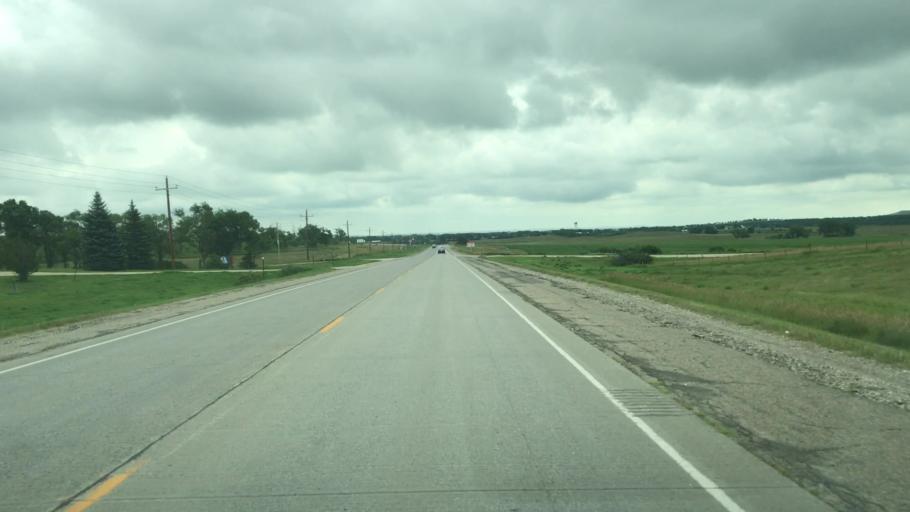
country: US
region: South Dakota
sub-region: Todd County
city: Mission
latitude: 43.3028
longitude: -100.6931
